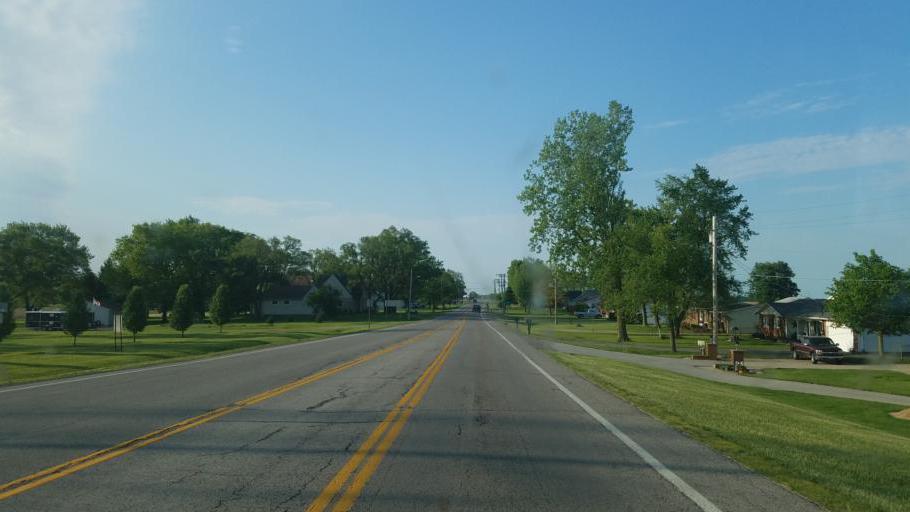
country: US
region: Ohio
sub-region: Fayette County
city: Washington Court House
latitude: 39.5131
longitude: -83.4424
